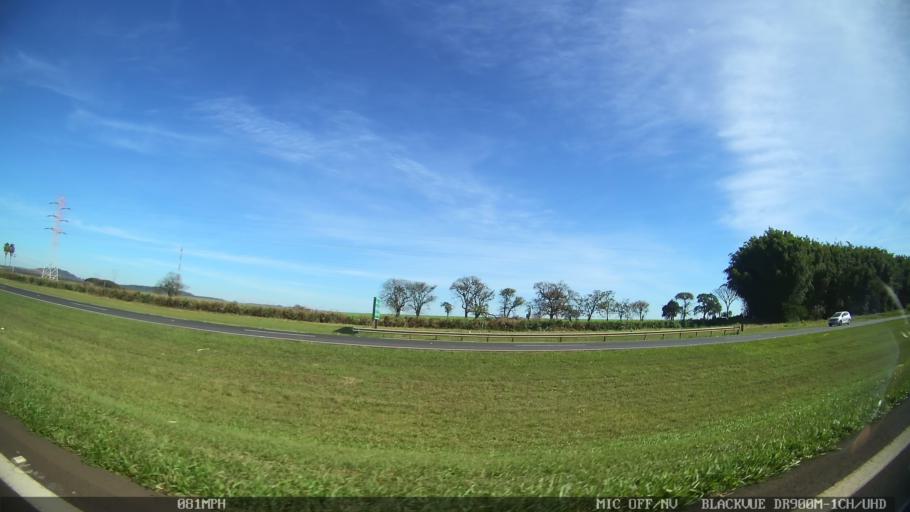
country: BR
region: Sao Paulo
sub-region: Araras
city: Araras
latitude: -22.2841
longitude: -47.3935
